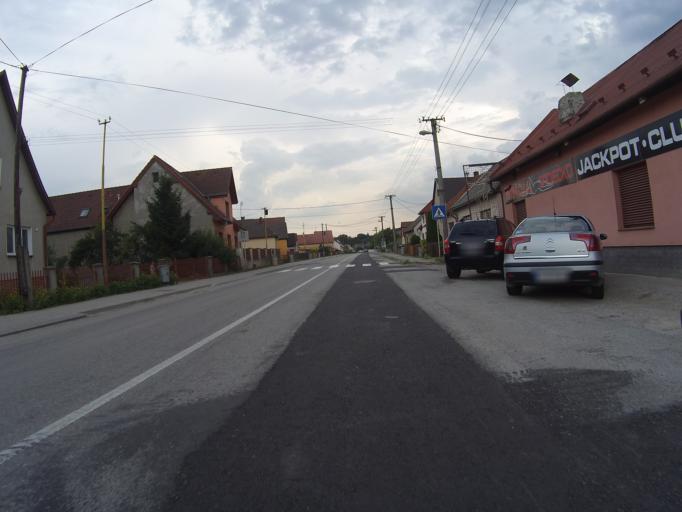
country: SK
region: Nitriansky
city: Ilava
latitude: 49.0396
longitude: 18.2898
